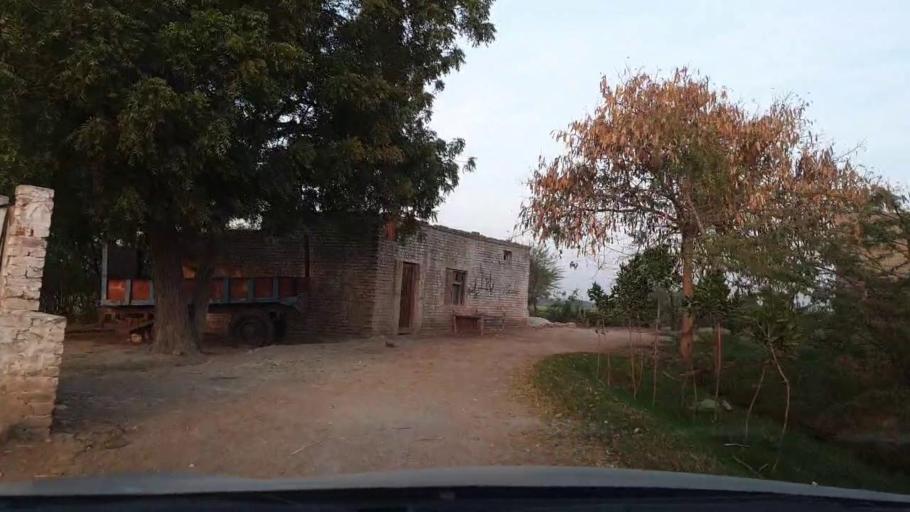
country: PK
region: Sindh
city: Tando Adam
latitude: 25.6799
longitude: 68.7012
